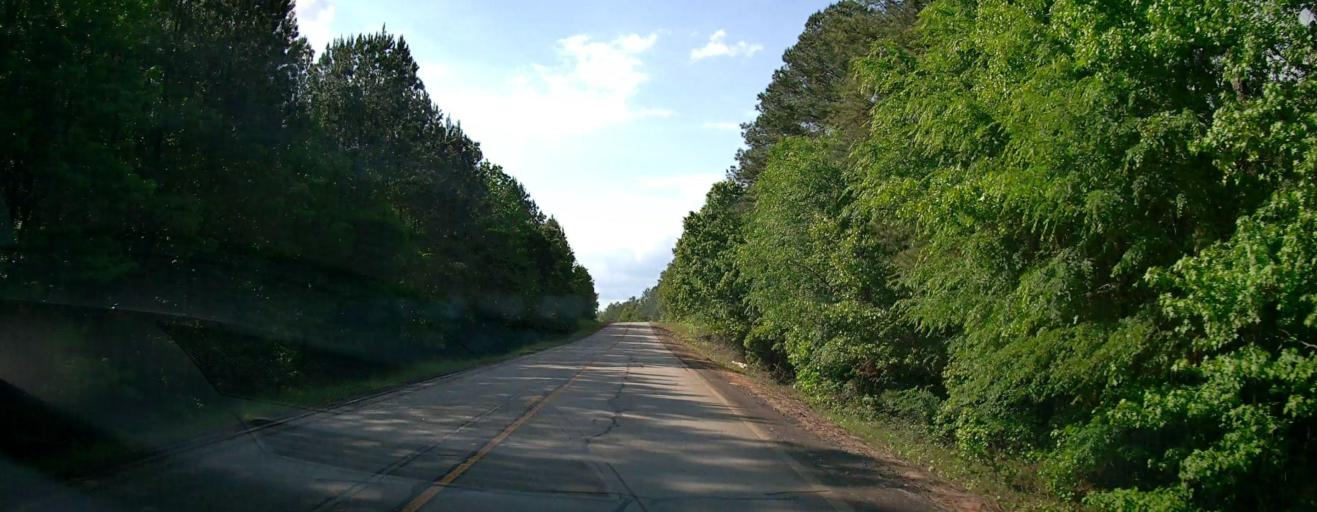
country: US
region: Georgia
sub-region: Washington County
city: Tennille
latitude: 32.9236
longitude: -83.0034
